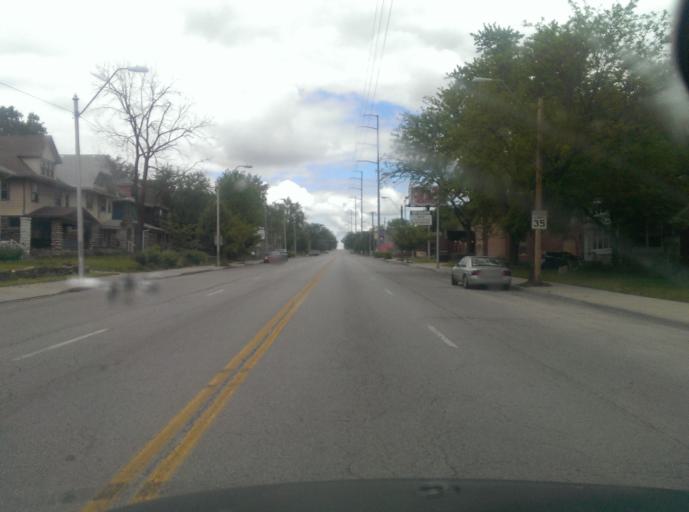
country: US
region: Kansas
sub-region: Johnson County
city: Westwood
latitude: 39.0456
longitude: -94.5728
